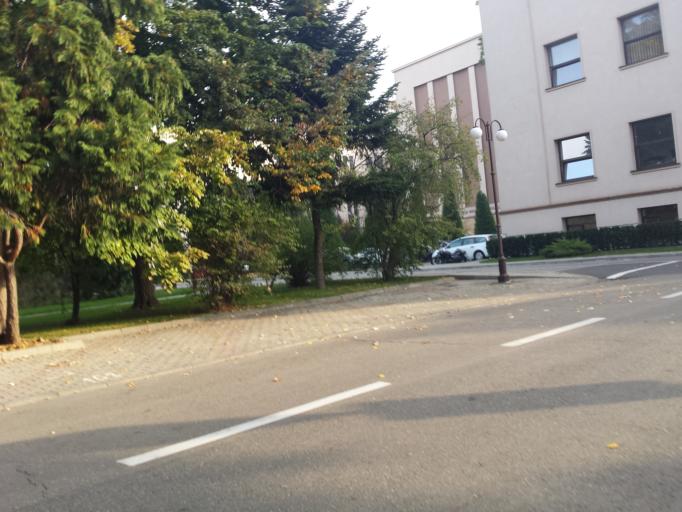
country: RO
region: Bucuresti
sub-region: Municipiul Bucuresti
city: Bucuresti
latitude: 44.4704
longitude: 26.0703
